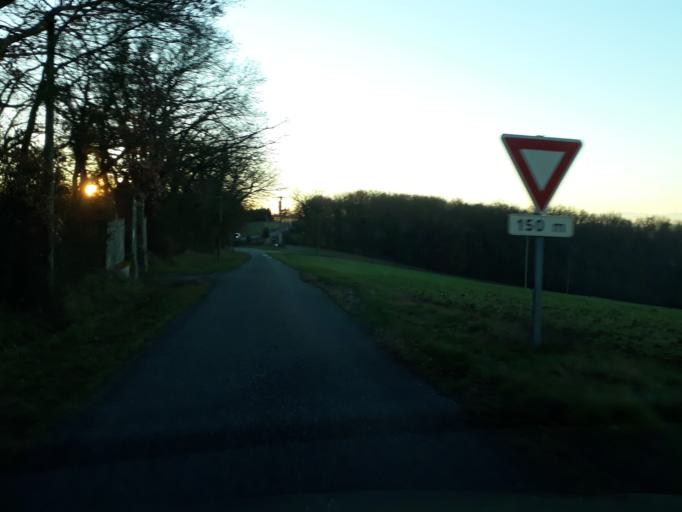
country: FR
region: Midi-Pyrenees
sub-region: Departement du Gers
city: Pavie
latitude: 43.6091
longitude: 0.6823
